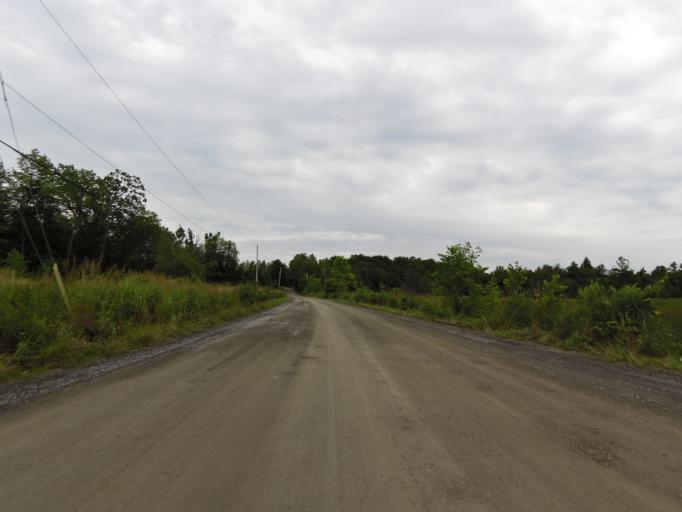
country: CA
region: Ontario
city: Kingston
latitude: 44.5605
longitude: -76.6281
